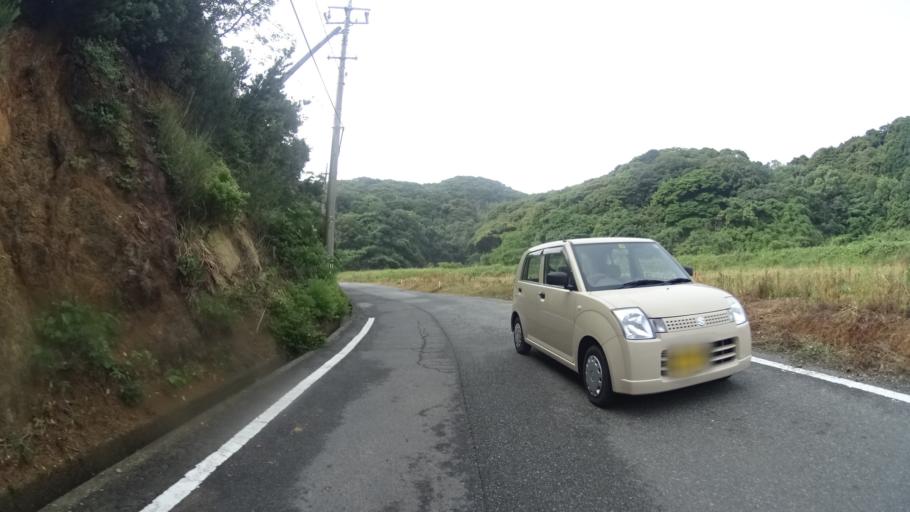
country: JP
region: Yamaguchi
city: Shimonoseki
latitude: 34.0972
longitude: 130.8757
